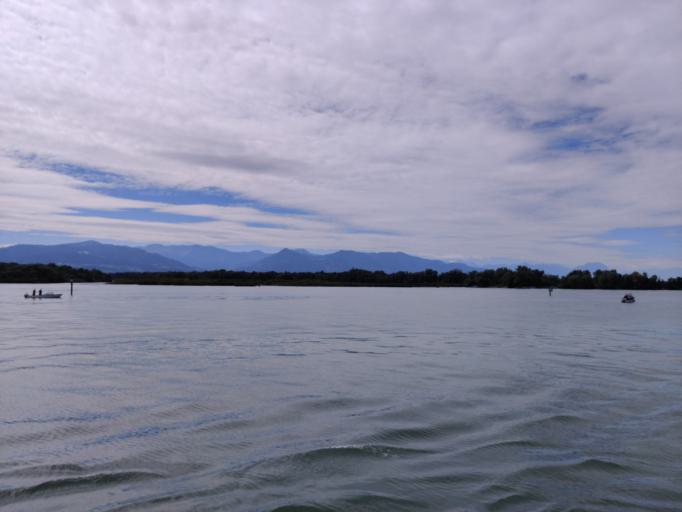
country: AT
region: Vorarlberg
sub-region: Politischer Bezirk Bregenz
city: Hard
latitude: 47.5097
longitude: 9.6902
